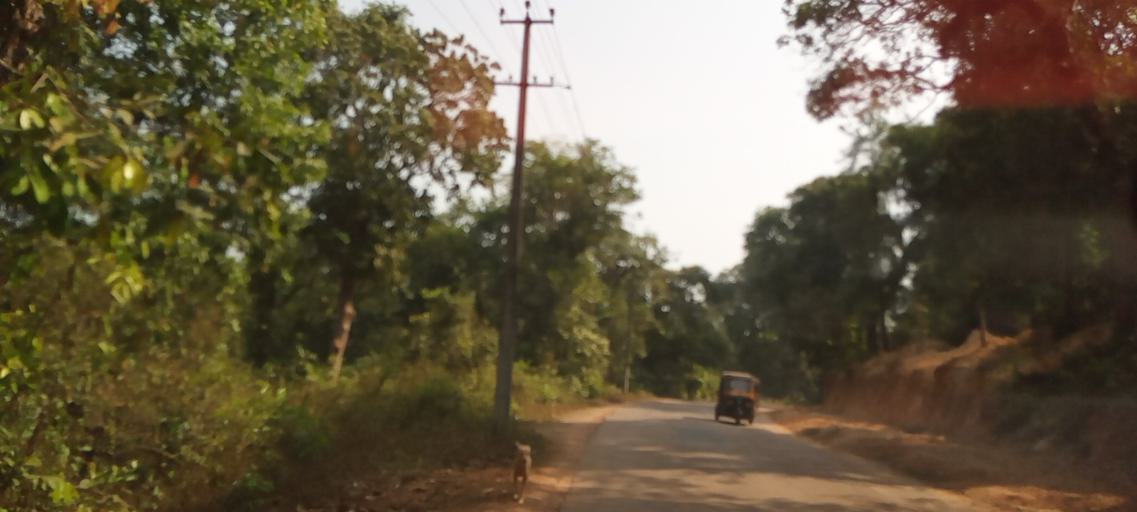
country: IN
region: Karnataka
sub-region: Udupi
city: Manipala
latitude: 13.5141
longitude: 74.8422
